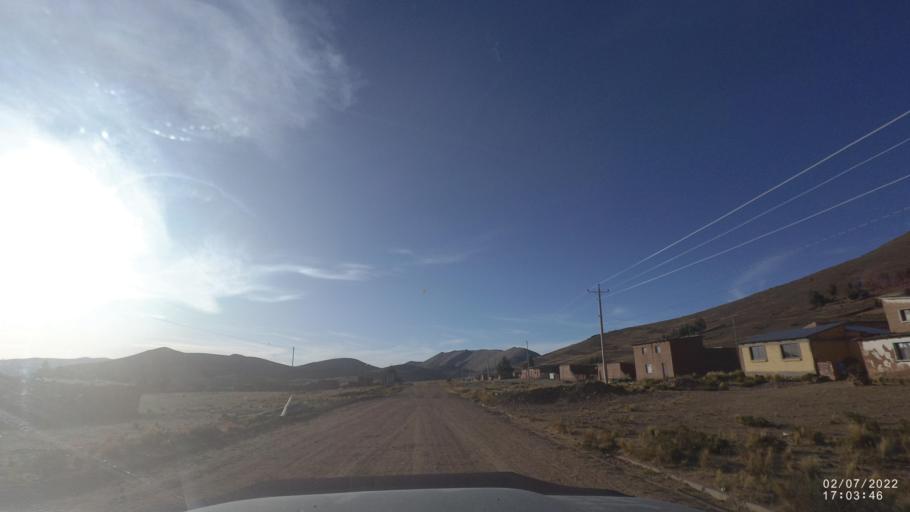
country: BO
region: Cochabamba
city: Irpa Irpa
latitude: -17.9211
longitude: -66.5572
